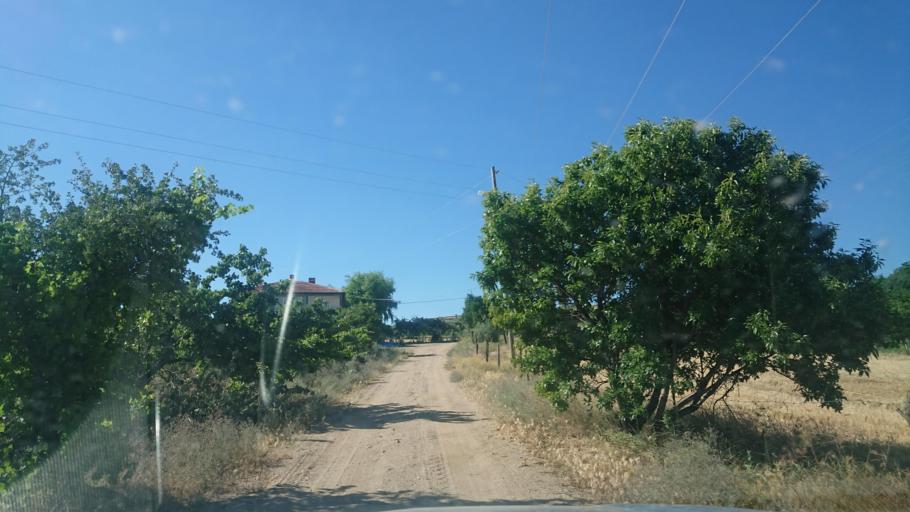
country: TR
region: Aksaray
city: Agacoren
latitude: 38.8569
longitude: 33.9442
